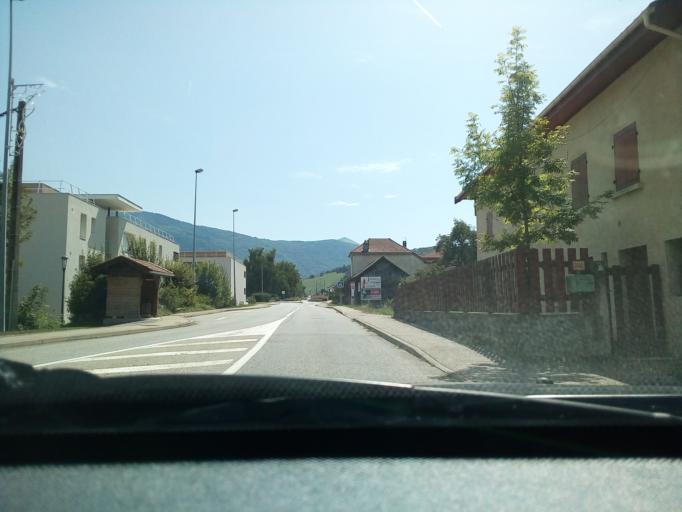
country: FR
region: Rhone-Alpes
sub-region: Departement de l'Isere
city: Brie-et-Angonnes
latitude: 45.1181
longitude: 5.7826
